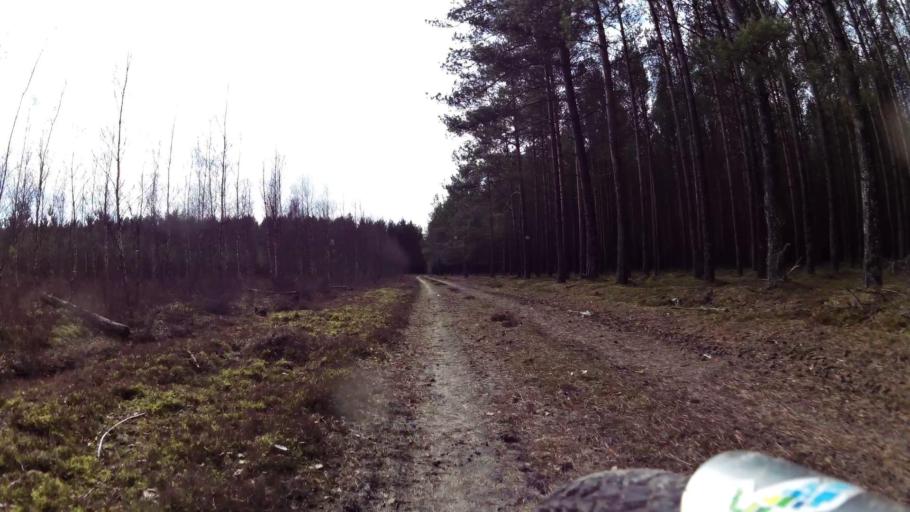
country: PL
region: Pomeranian Voivodeship
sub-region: Powiat bytowski
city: Kolczyglowy
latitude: 54.1891
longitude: 17.2131
